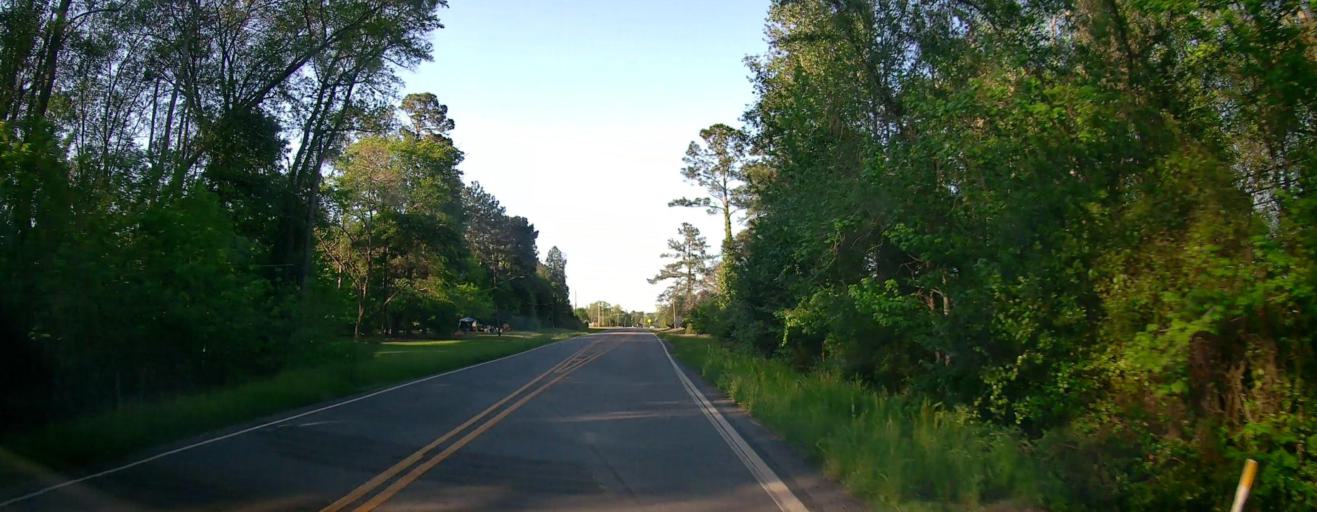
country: US
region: Georgia
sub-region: Macon County
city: Oglethorpe
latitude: 32.2852
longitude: -84.0702
